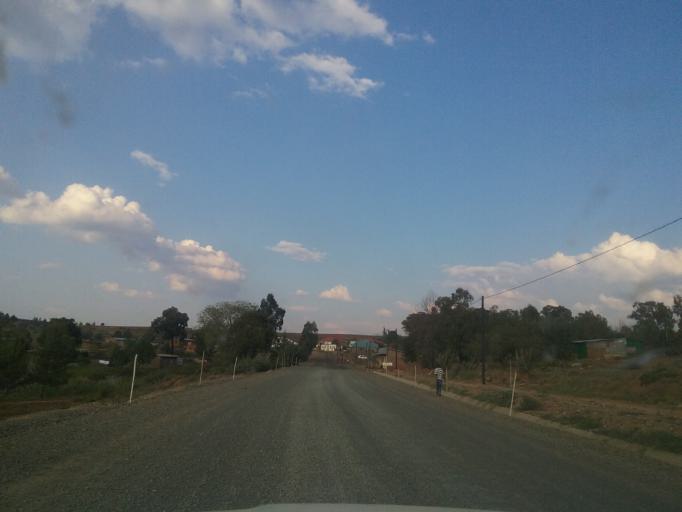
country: LS
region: Quthing
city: Quthing
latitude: -30.3948
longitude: 27.6211
